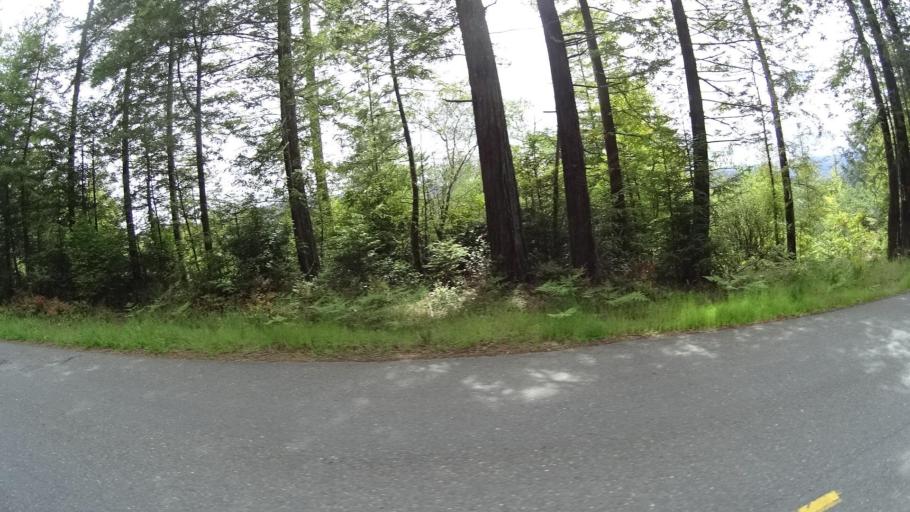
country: US
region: California
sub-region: Humboldt County
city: Bayside
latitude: 40.7854
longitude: -124.0574
